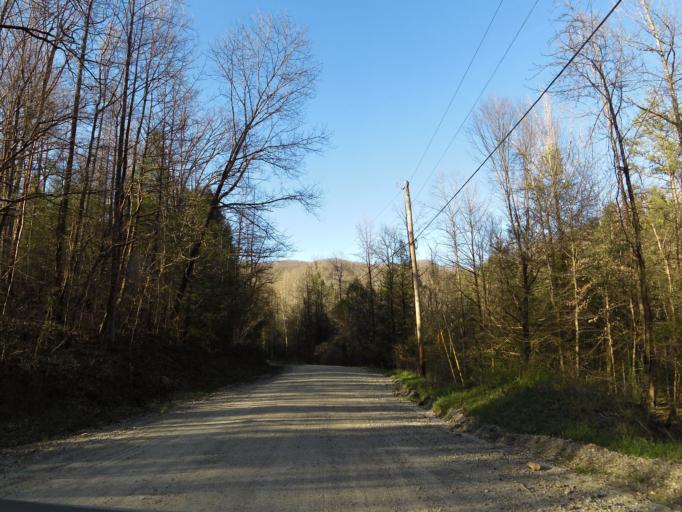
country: US
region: Tennessee
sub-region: Scott County
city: Huntsville
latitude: 36.2408
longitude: -84.4128
